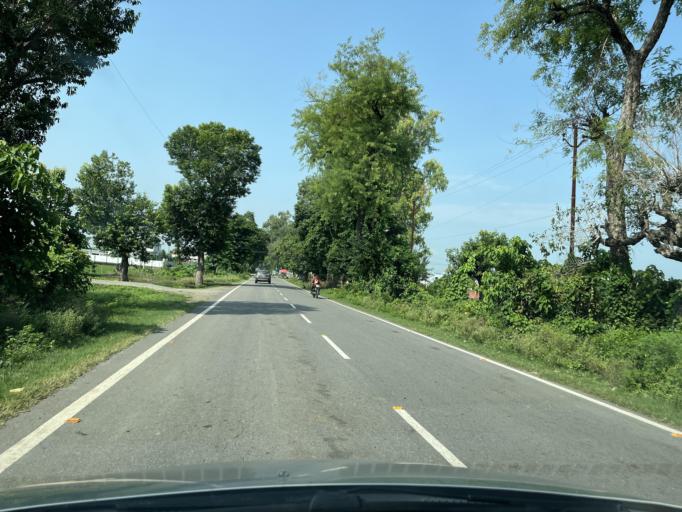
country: IN
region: Uttarakhand
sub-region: Udham Singh Nagar
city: Bazpur
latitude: 29.2143
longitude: 79.2231
